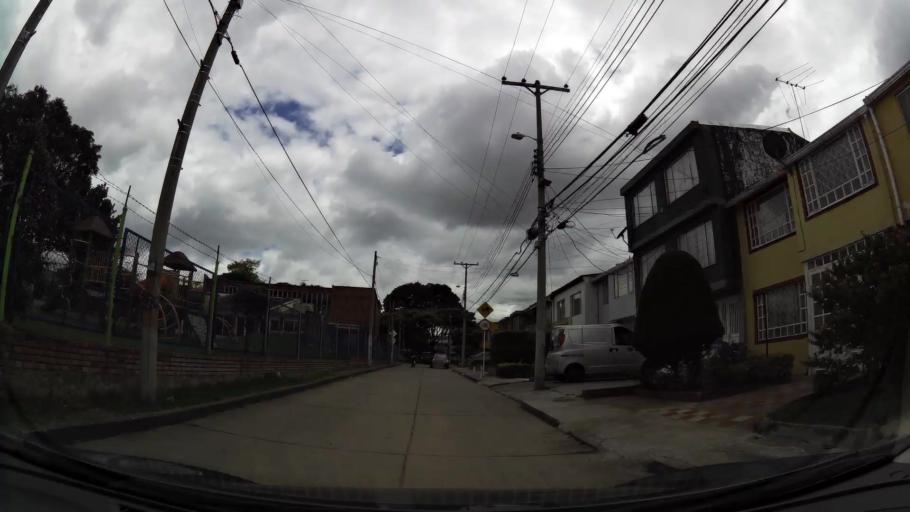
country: CO
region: Bogota D.C.
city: Barrio San Luis
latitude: 4.7029
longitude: -74.0950
